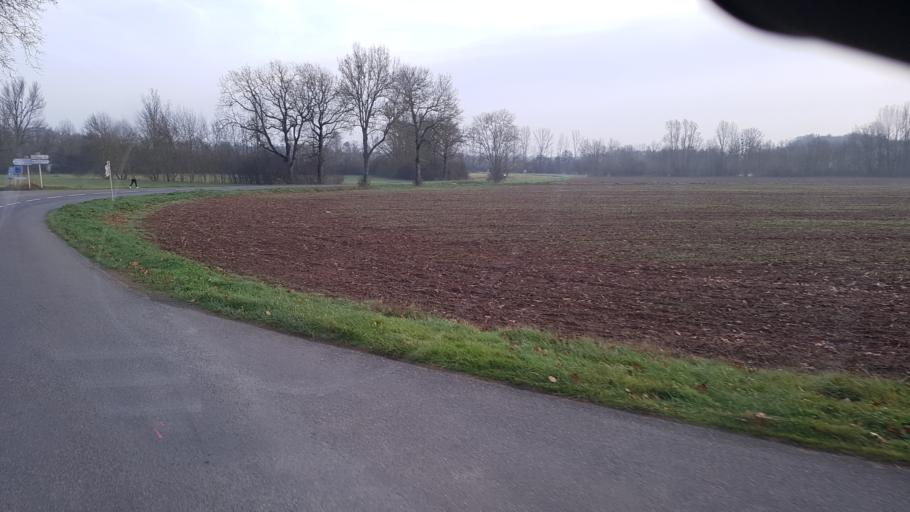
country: FR
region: Midi-Pyrenees
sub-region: Departement du Tarn
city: Cahuzac-sur-Vere
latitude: 43.9826
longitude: 1.8137
